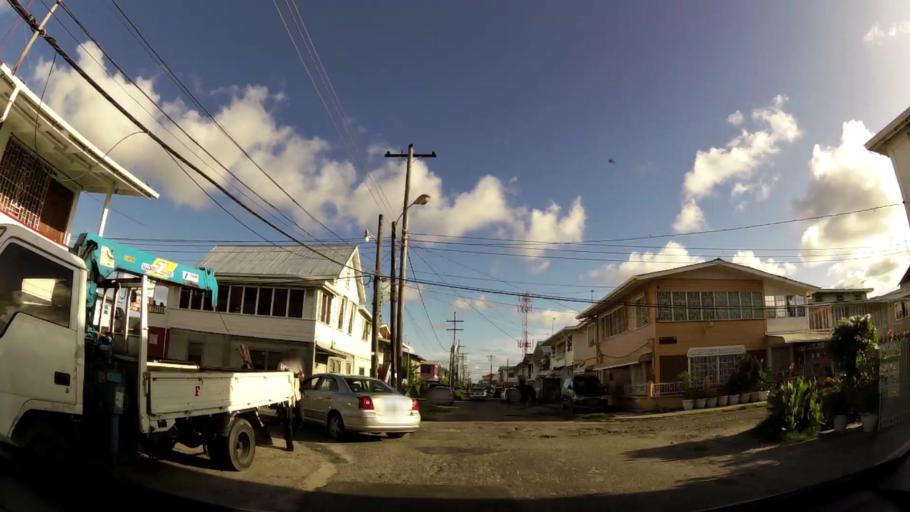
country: GY
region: Demerara-Mahaica
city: Georgetown
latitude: 6.8162
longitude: -58.1531
